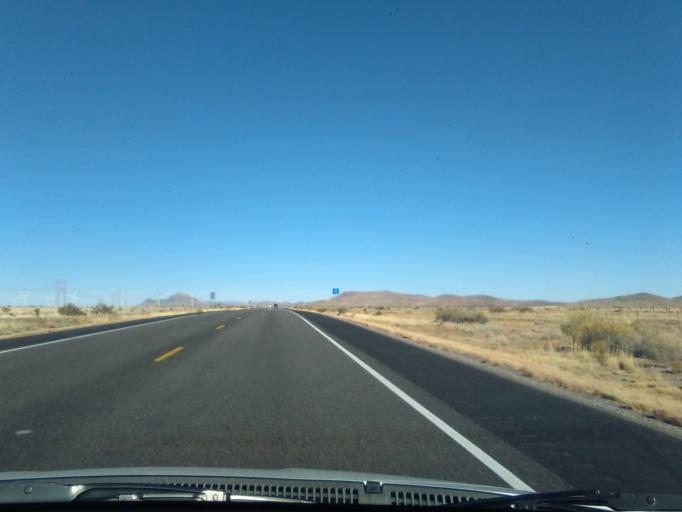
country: US
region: New Mexico
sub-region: Luna County
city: Deming
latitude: 32.4904
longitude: -107.5205
